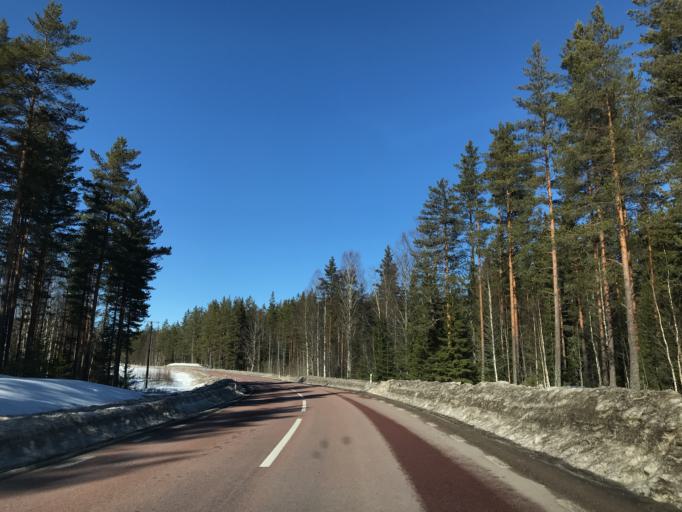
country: SE
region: Vaermland
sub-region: Filipstads Kommun
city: Lesjofors
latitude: 60.1552
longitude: 14.2111
